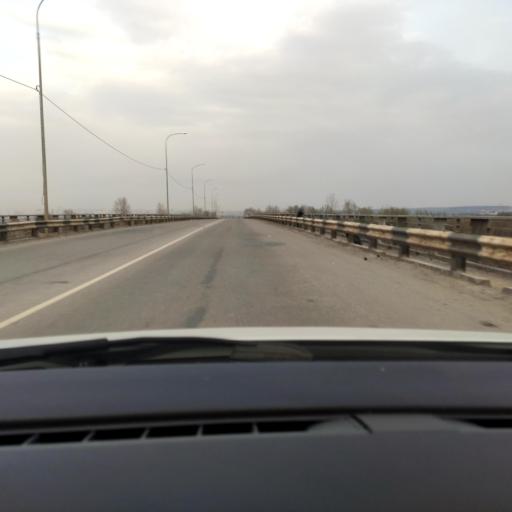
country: RU
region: Voronezj
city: Pridonskoy
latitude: 51.7239
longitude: 39.0606
